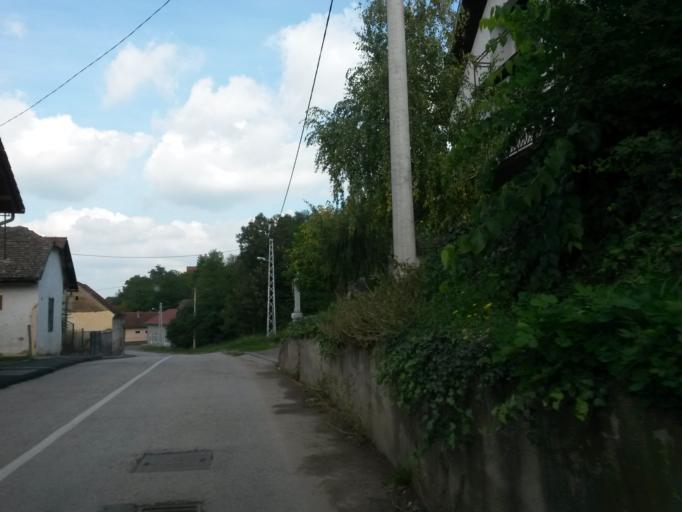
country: HR
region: Vukovarsko-Srijemska
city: Ilok
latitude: 45.2192
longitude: 19.3814
